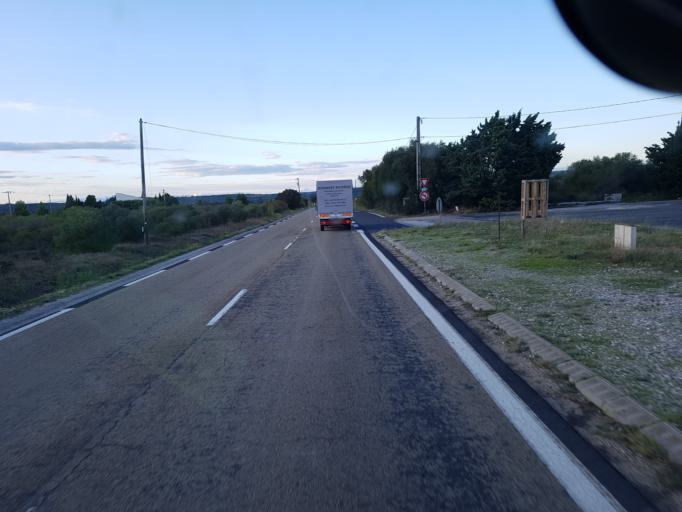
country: FR
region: Languedoc-Roussillon
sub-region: Departement de l'Aude
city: Leucate
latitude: 42.9454
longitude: 2.9886
